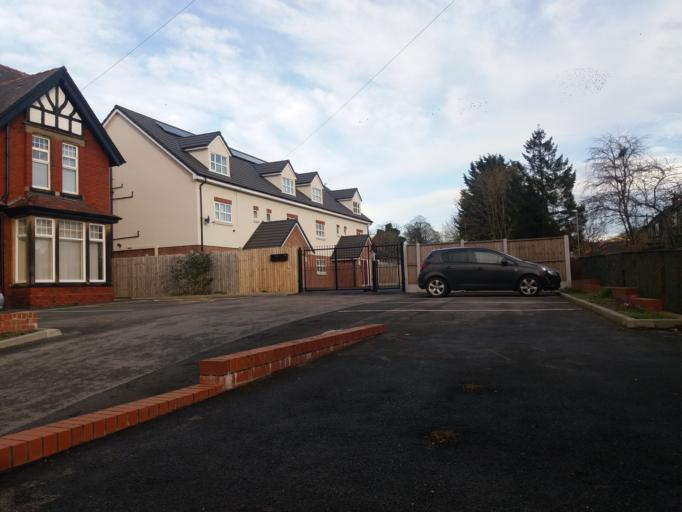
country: GB
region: England
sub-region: Lancashire
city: Chorley
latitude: 53.6558
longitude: -2.6245
